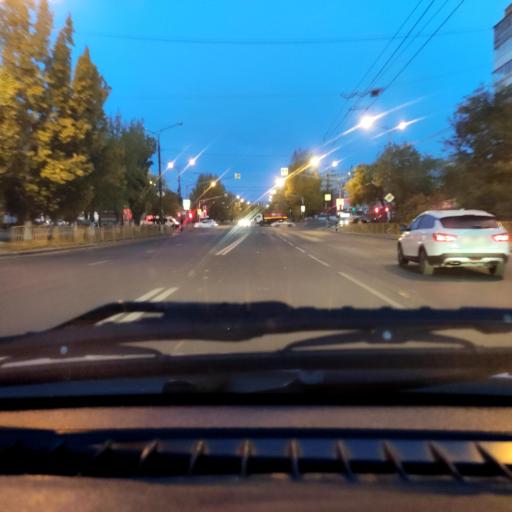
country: RU
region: Samara
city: Zhigulevsk
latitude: 53.4815
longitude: 49.4757
